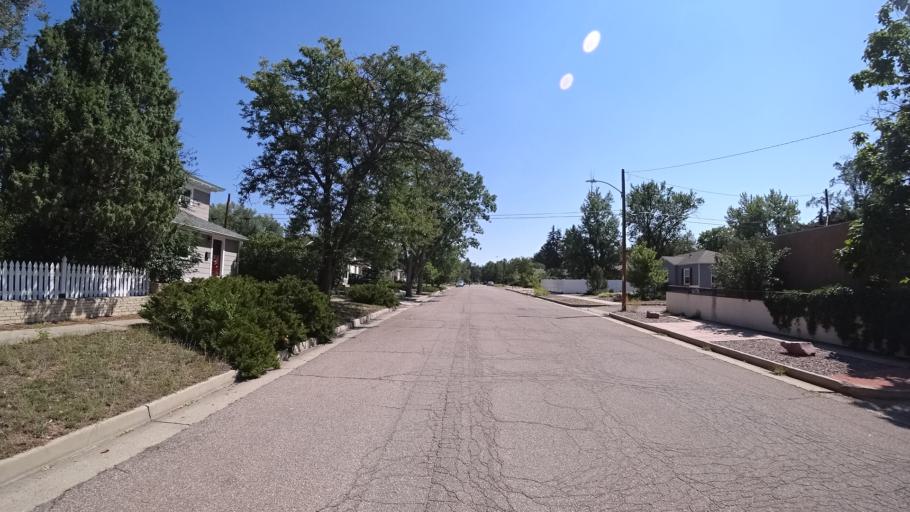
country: US
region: Colorado
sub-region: El Paso County
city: Colorado Springs
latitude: 38.8515
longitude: -104.8053
